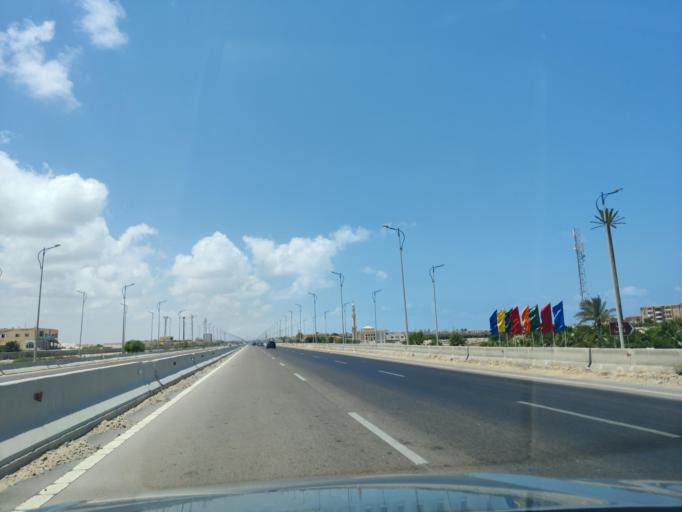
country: EG
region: Muhafazat Matruh
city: Al `Alamayn
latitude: 30.9078
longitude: 29.4316
